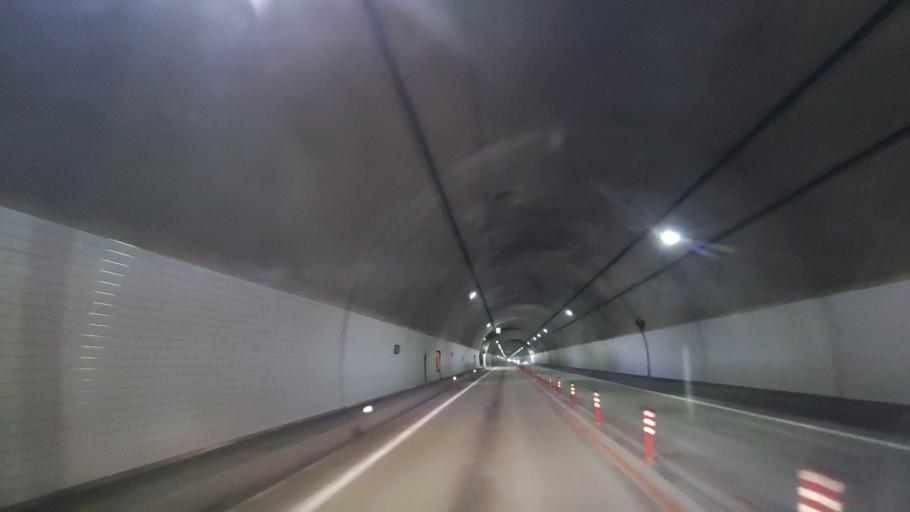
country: JP
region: Akita
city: Odate
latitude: 40.3530
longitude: 140.6830
